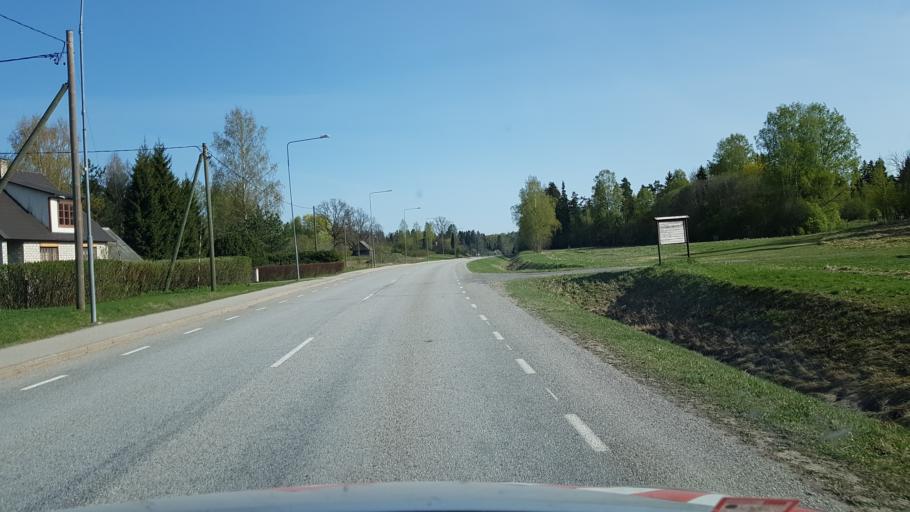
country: EE
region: Viljandimaa
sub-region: Abja vald
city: Abja-Paluoja
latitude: 58.1311
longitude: 25.3641
